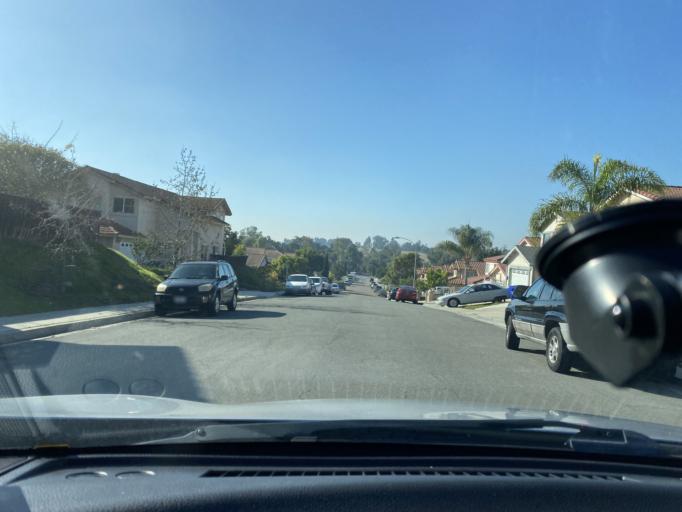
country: US
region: California
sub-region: San Diego County
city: National City
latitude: 32.7060
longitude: -117.0907
